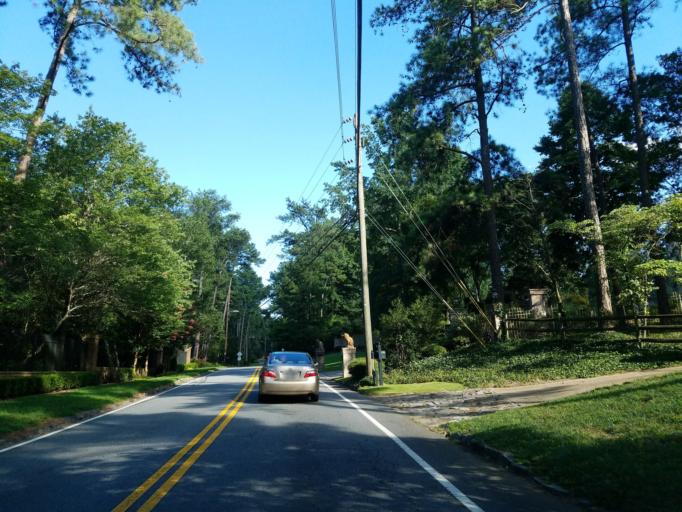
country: US
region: Georgia
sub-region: Fulton County
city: Sandy Springs
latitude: 33.9273
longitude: -84.4113
